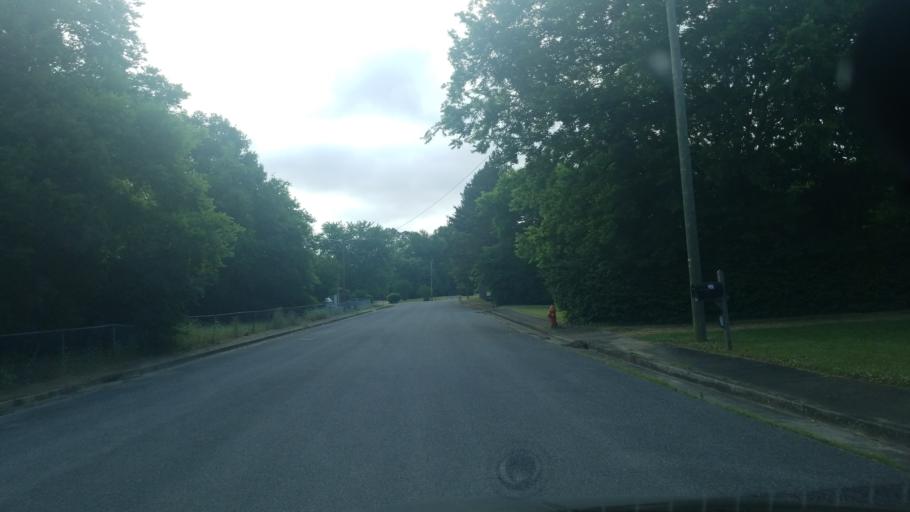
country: US
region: Tennessee
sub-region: Davidson County
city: Nashville
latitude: 36.2315
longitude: -86.7454
